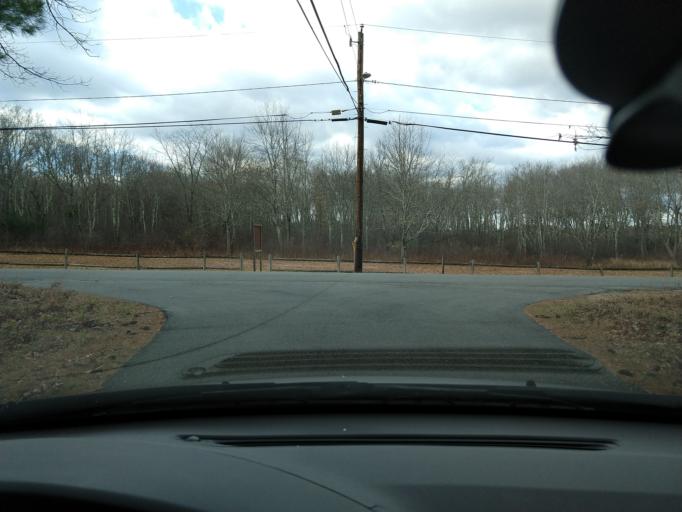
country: US
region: Massachusetts
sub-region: Middlesex County
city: Wayland
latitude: 42.4017
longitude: -71.3751
